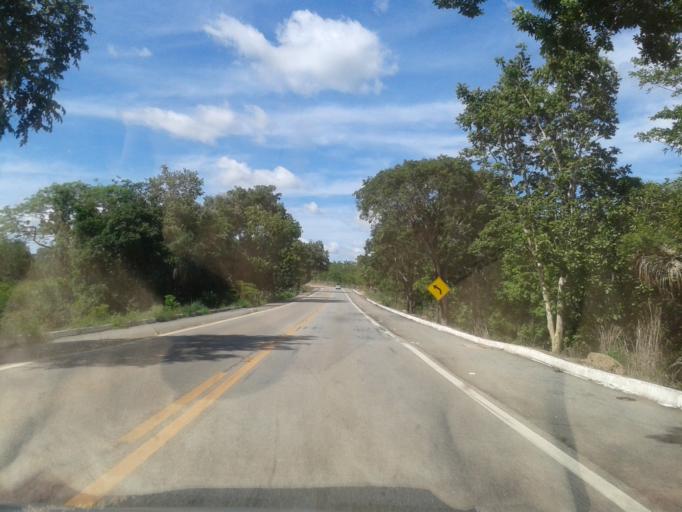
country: BR
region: Goias
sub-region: Itapuranga
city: Itapuranga
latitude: -15.3777
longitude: -50.3881
